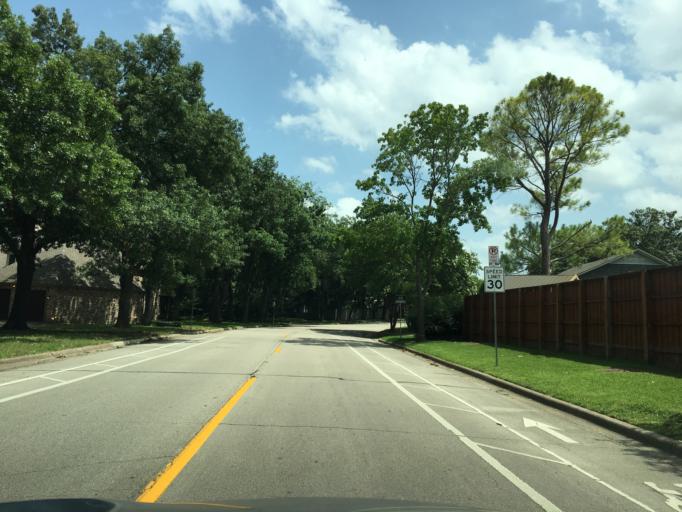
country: US
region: Texas
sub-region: Dallas County
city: University Park
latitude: 32.8841
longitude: -96.7774
